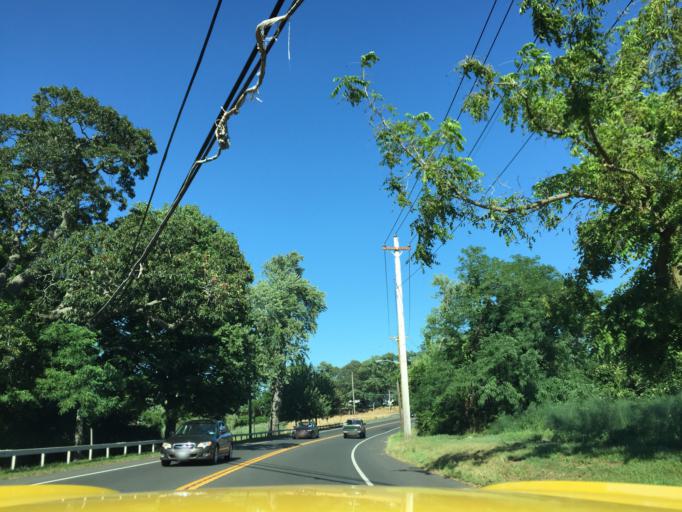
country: US
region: New York
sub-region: Suffolk County
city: Aquebogue
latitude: 40.9479
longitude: -72.6164
